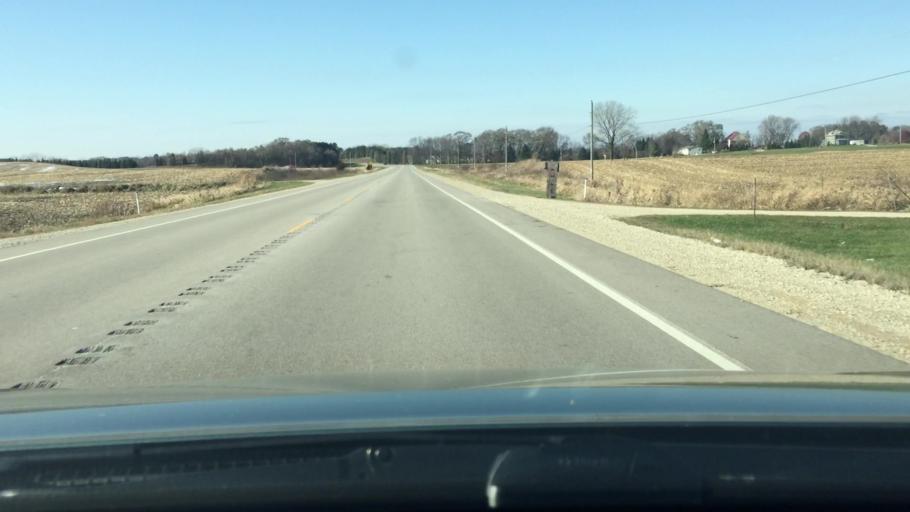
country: US
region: Wisconsin
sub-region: Jefferson County
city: Lake Ripley
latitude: 43.0104
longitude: -88.9581
